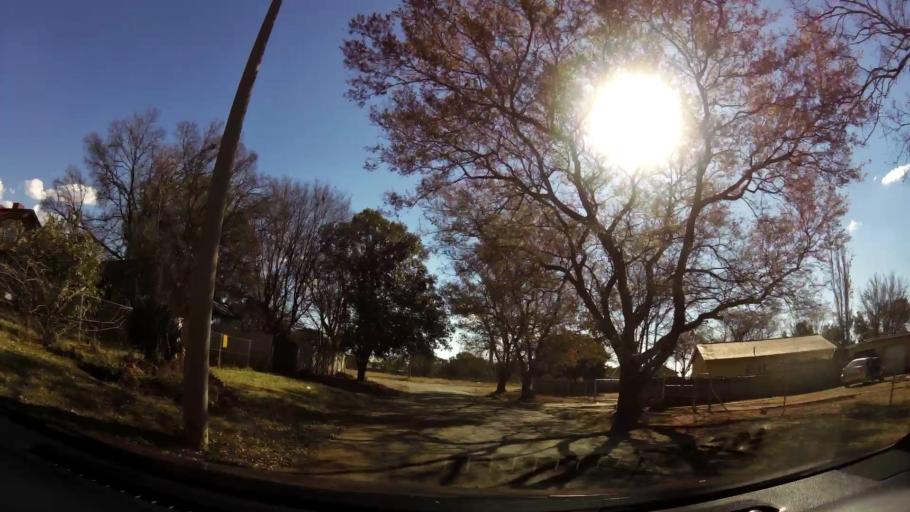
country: ZA
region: Gauteng
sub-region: West Rand District Municipality
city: Carletonville
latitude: -26.3608
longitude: 27.3707
